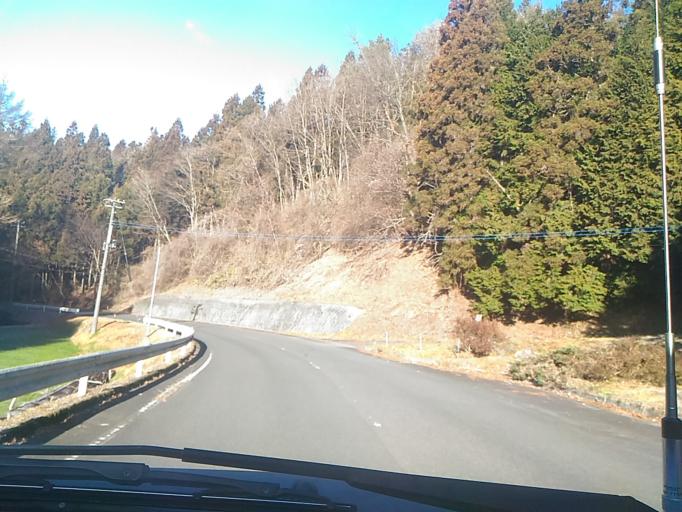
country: JP
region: Fukushima
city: Ishikawa
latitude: 37.0220
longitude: 140.5268
